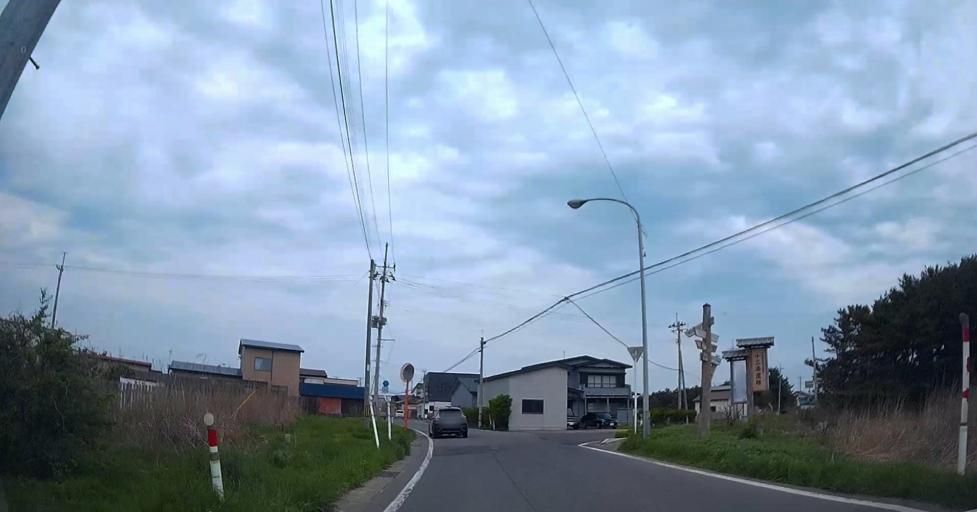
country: JP
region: Aomori
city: Shimokizukuri
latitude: 41.0249
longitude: 140.3286
